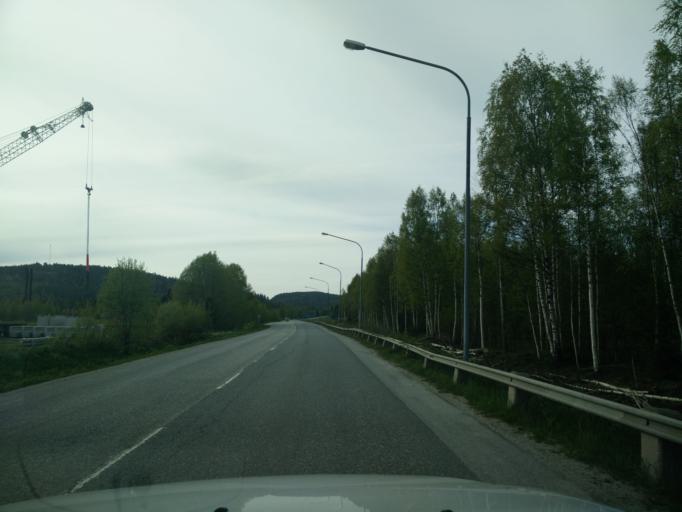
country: SE
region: Vaesternorrland
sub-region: OErnskoeldsviks Kommun
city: Bjasta
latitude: 63.1998
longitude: 18.4965
